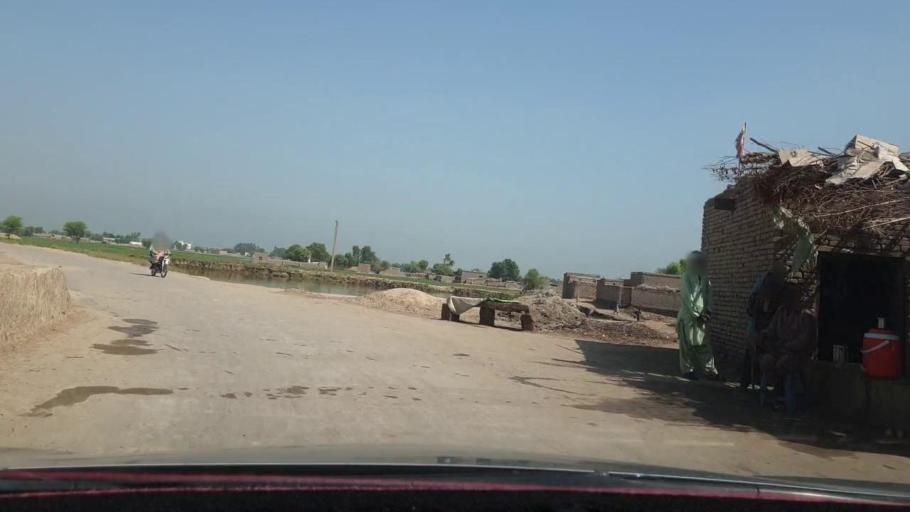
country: PK
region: Sindh
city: Warah
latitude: 27.4761
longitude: 67.8331
